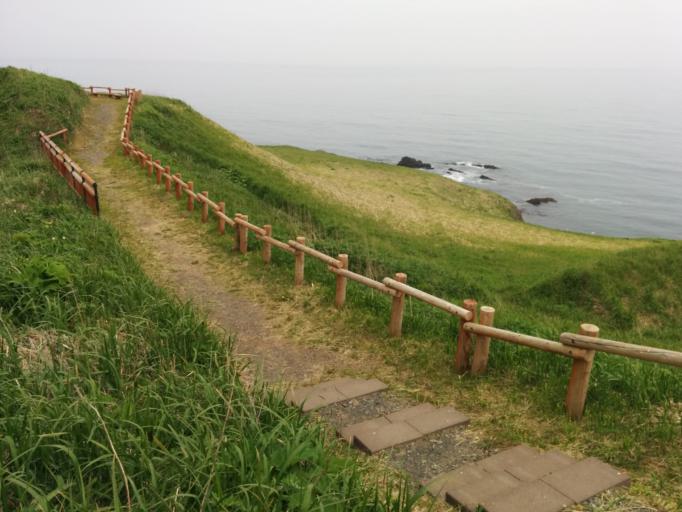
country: JP
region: Hokkaido
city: Nemuro
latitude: 43.0769
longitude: 145.1691
